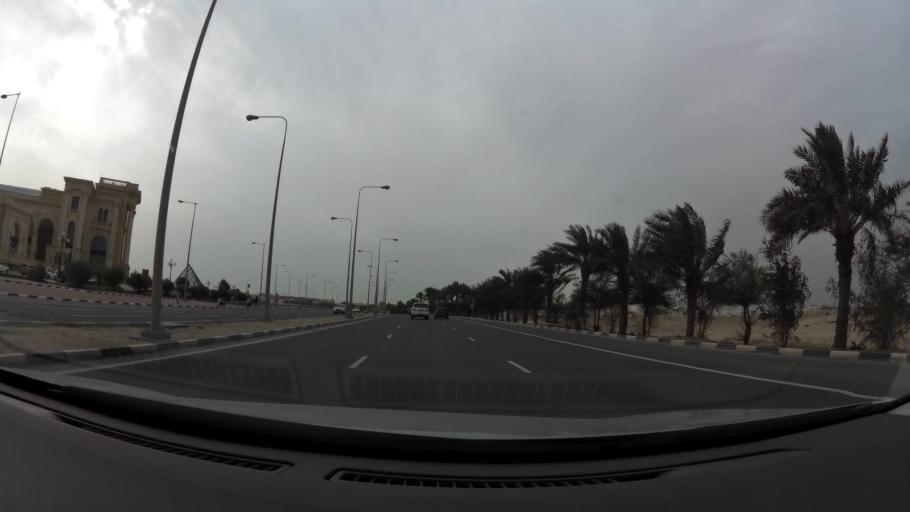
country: QA
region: Baladiyat ad Dawhah
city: Doha
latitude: 25.3333
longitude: 51.4977
